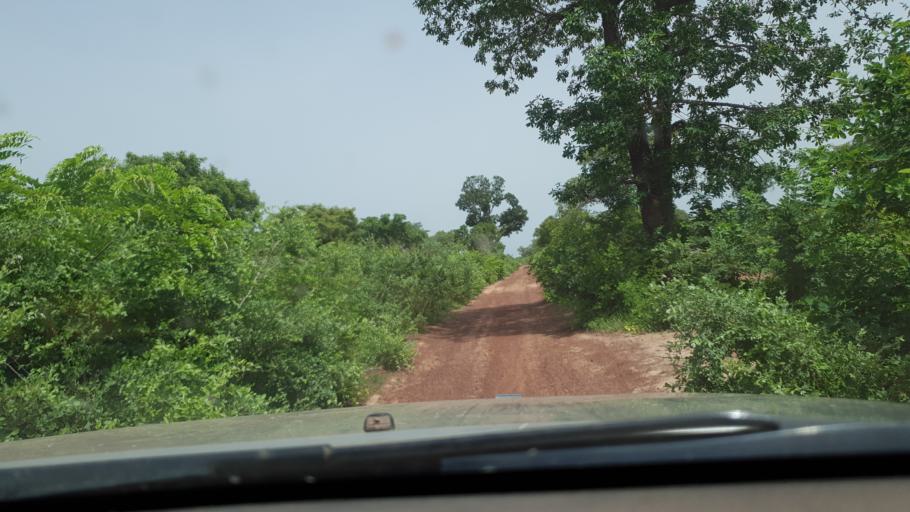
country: ML
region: Koulikoro
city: Koulikoro
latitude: 12.6646
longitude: -7.2167
